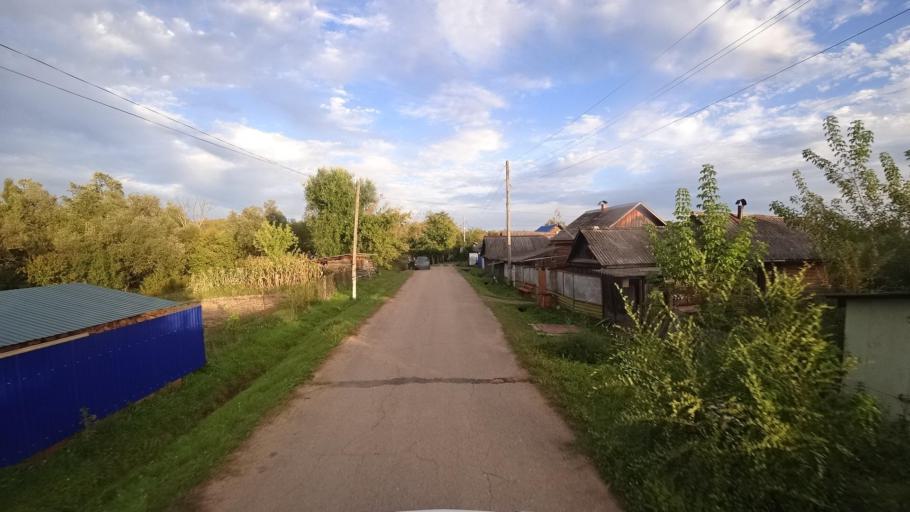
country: RU
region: Primorskiy
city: Yakovlevka
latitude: 44.4231
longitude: 133.4888
